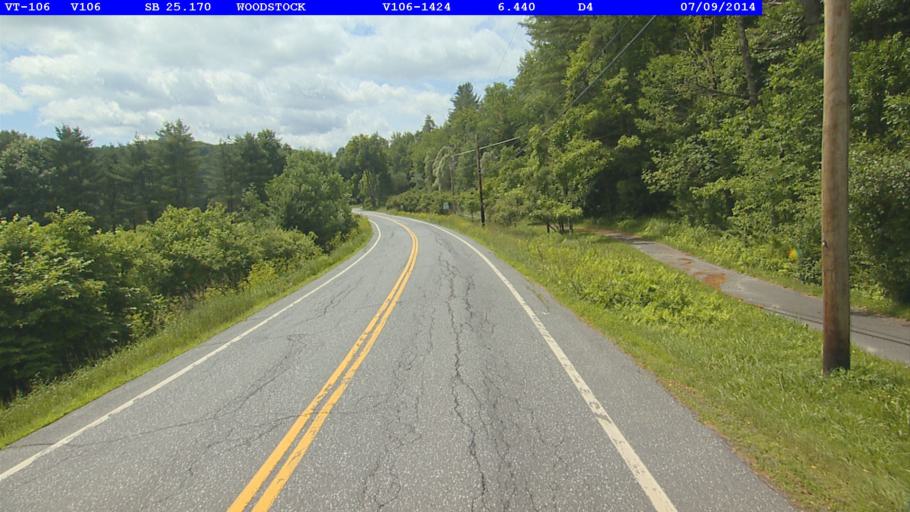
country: US
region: Vermont
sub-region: Windsor County
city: Woodstock
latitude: 43.6128
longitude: -72.5174
